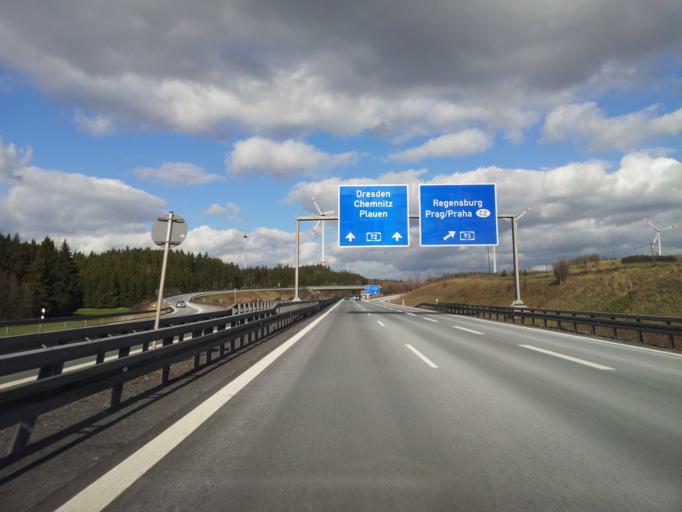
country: DE
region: Bavaria
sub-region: Upper Franconia
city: Trogen
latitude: 50.3805
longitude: 11.9548
